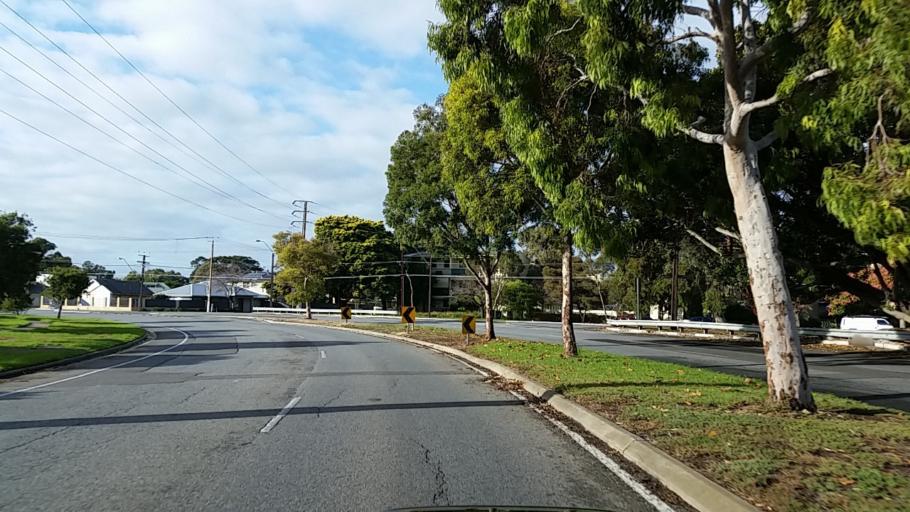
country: AU
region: South Australia
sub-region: Charles Sturt
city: Henley Beach
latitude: -34.9263
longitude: 138.5067
